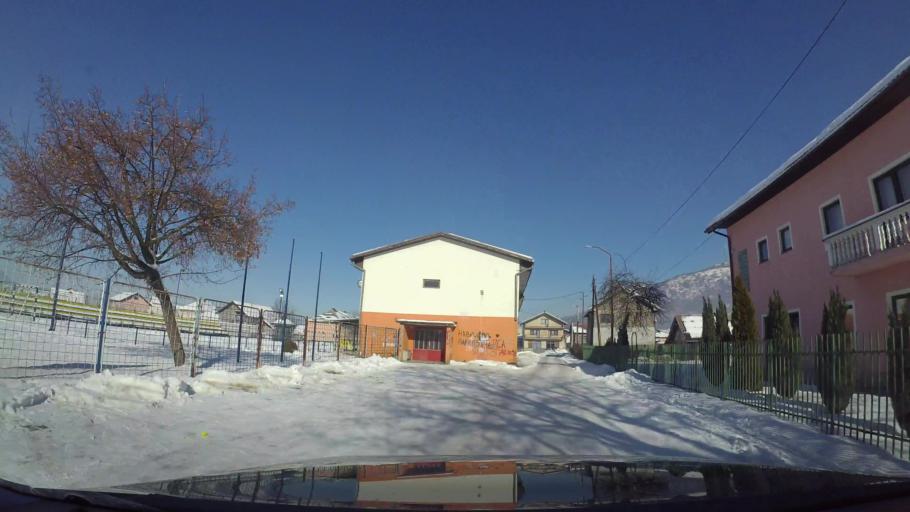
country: BA
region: Federation of Bosnia and Herzegovina
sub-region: Kanton Sarajevo
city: Sarajevo
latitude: 43.7984
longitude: 18.3472
